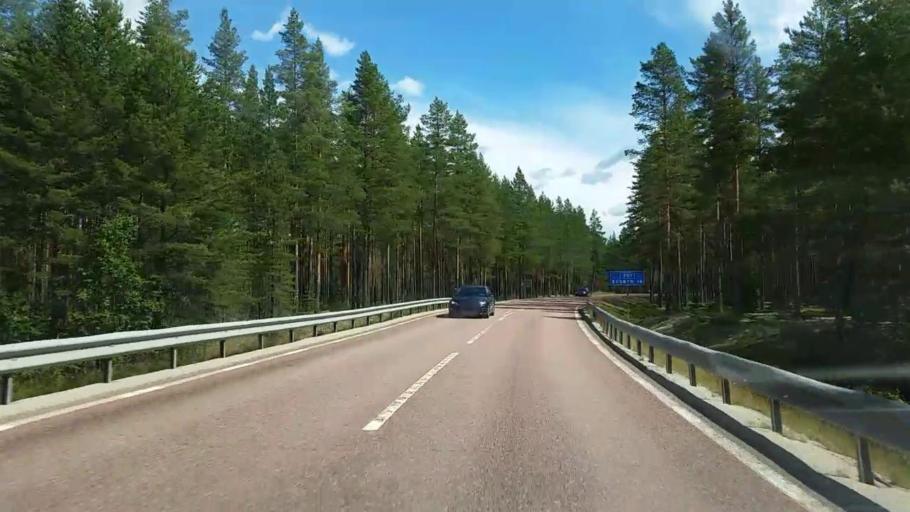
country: SE
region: Gaevleborg
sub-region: Ovanakers Kommun
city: Edsbyn
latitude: 61.3516
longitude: 15.5846
